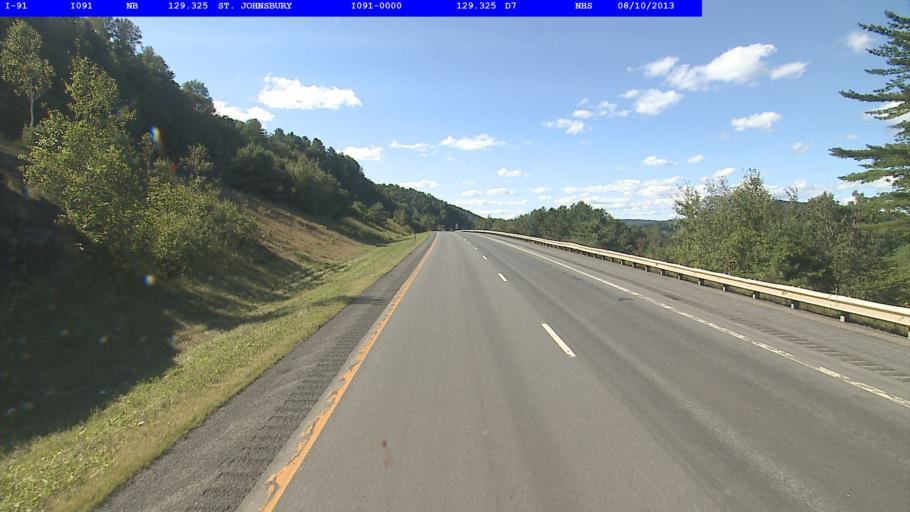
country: US
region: Vermont
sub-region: Caledonia County
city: Saint Johnsbury
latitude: 44.4104
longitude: -72.0269
